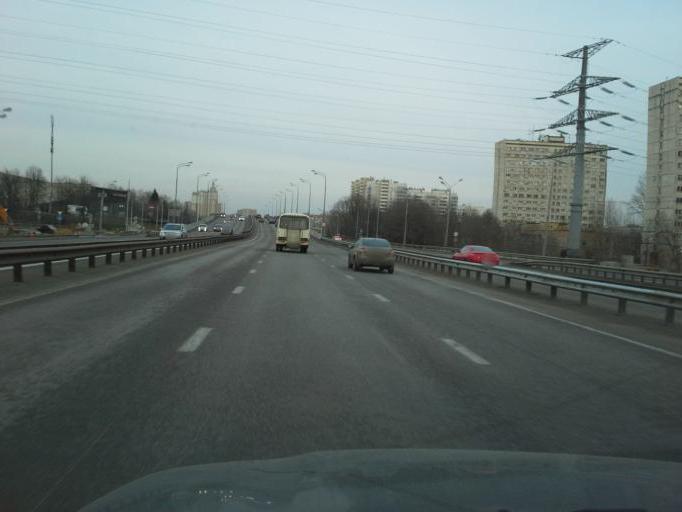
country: RU
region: Moskovskaya
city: Bol'shaya Setun'
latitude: 55.7152
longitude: 37.3977
